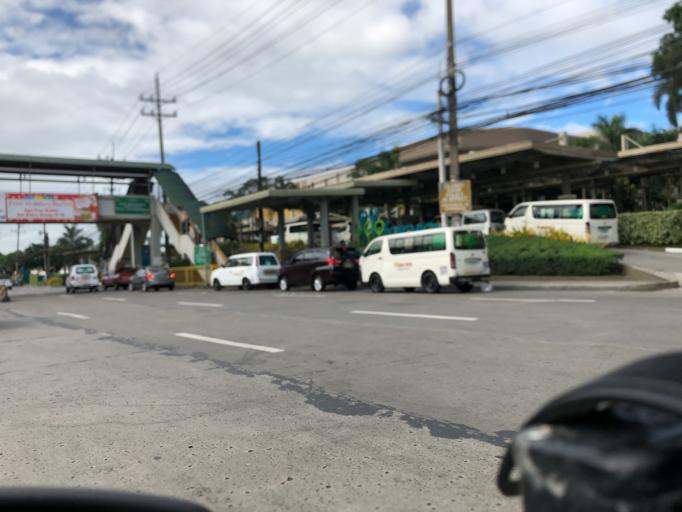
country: PH
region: Calabarzon
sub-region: Province of Rizal
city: San Mateo
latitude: 14.7354
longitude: 121.0605
